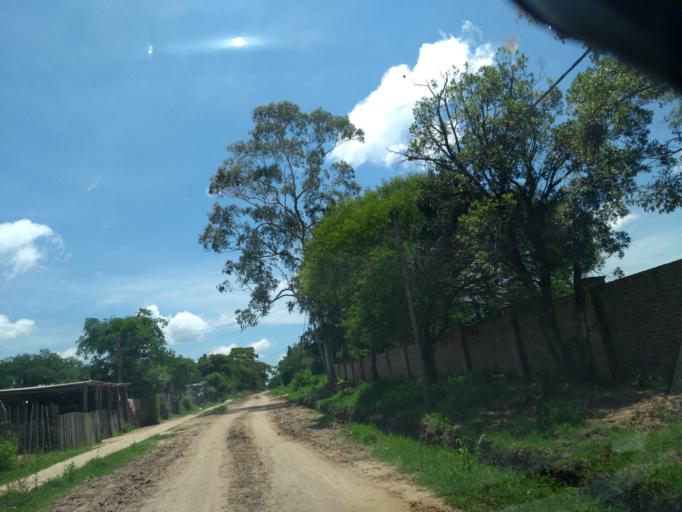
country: AR
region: Chaco
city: Resistencia
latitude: -27.4527
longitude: -58.9598
